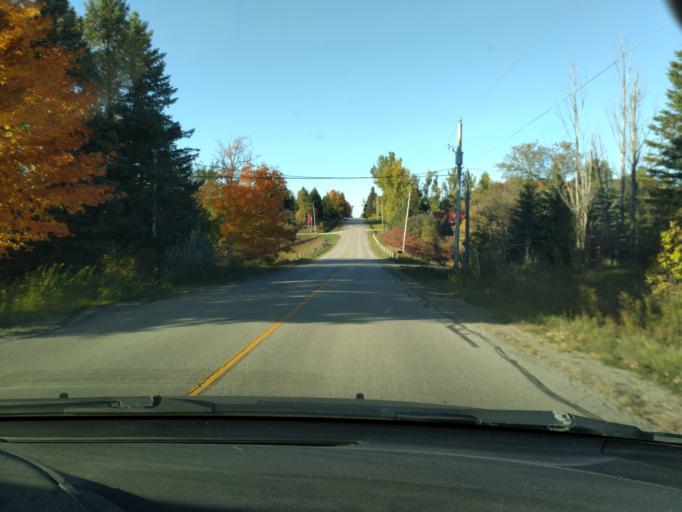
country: CA
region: Ontario
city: Bradford West Gwillimbury
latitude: 44.0039
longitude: -79.7224
